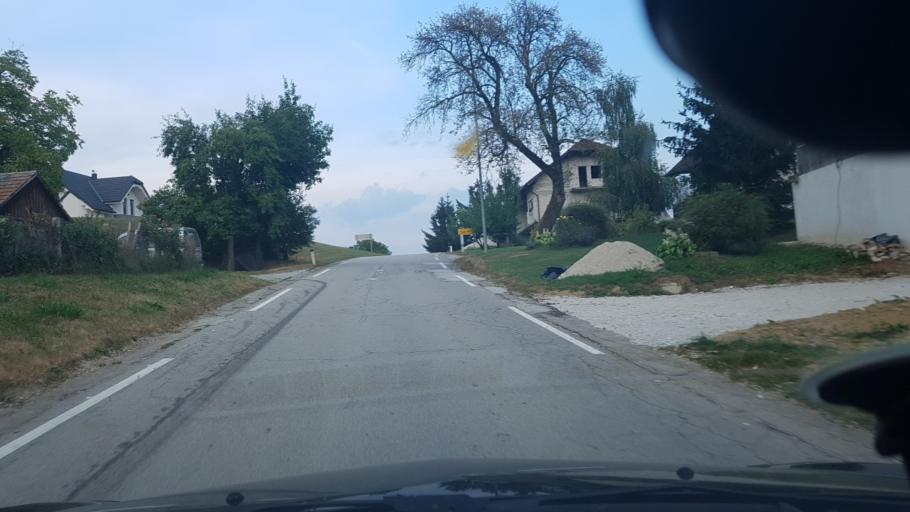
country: SI
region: Krsko
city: Senovo
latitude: 46.0360
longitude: 15.5258
